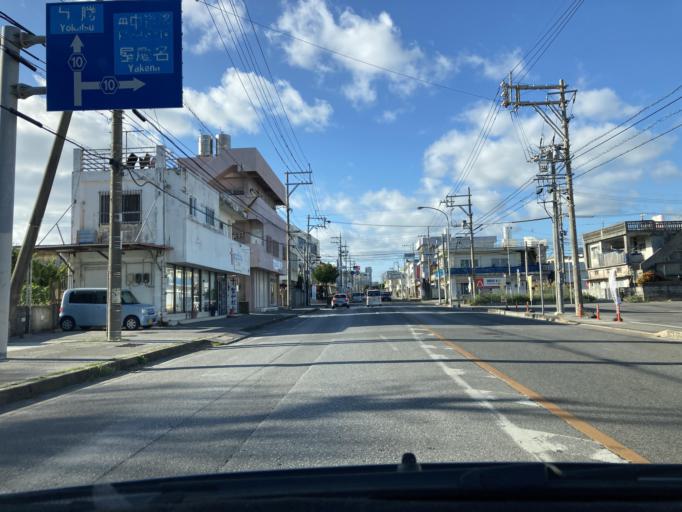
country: JP
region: Okinawa
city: Katsuren-haebaru
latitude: 26.3242
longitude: 127.8910
